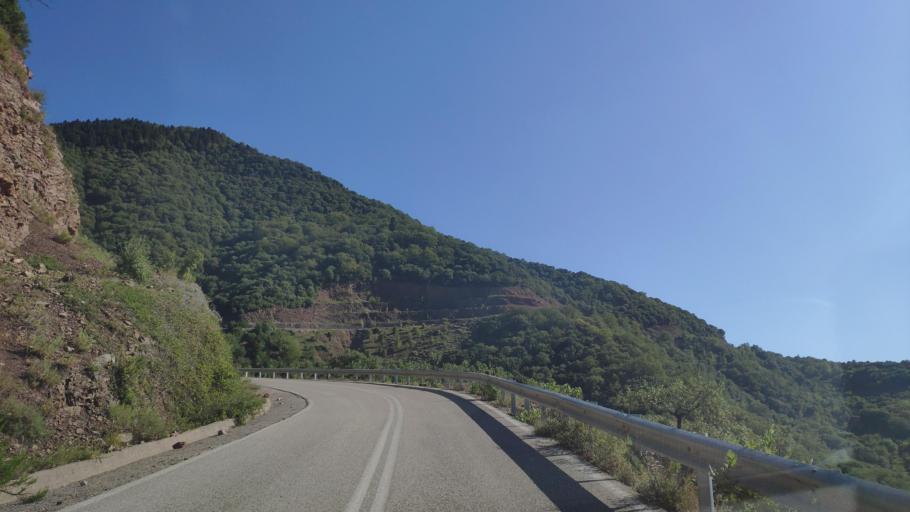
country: GR
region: Central Greece
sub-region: Nomos Evrytanias
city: Kerasochori
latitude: 39.0146
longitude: 21.5970
